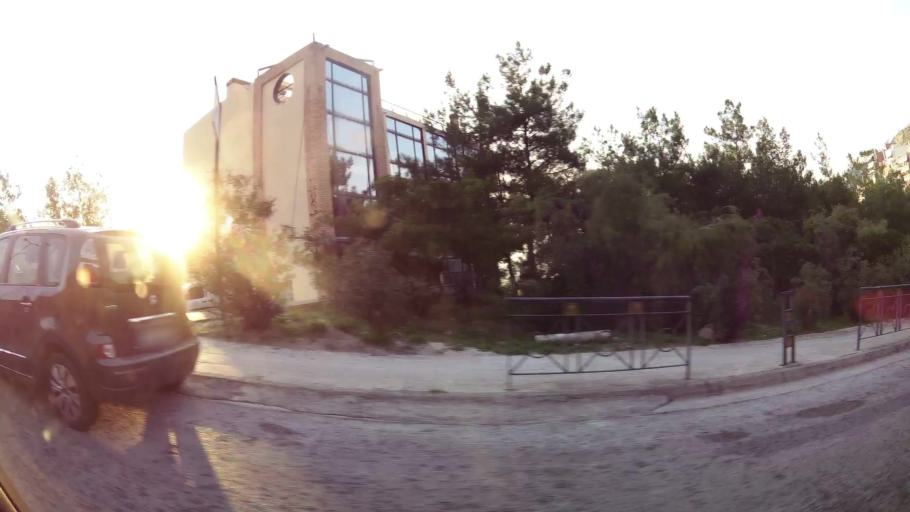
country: GR
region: Attica
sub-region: Nomarchia Athinas
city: Psychiko
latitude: 38.0080
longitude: 23.7613
